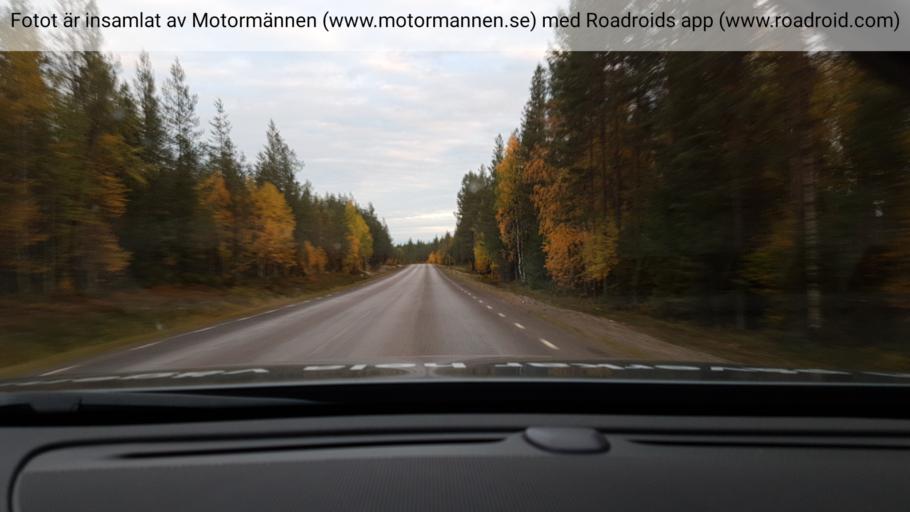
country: SE
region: Norrbotten
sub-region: Jokkmokks Kommun
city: Jokkmokk
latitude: 66.0029
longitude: 20.1610
